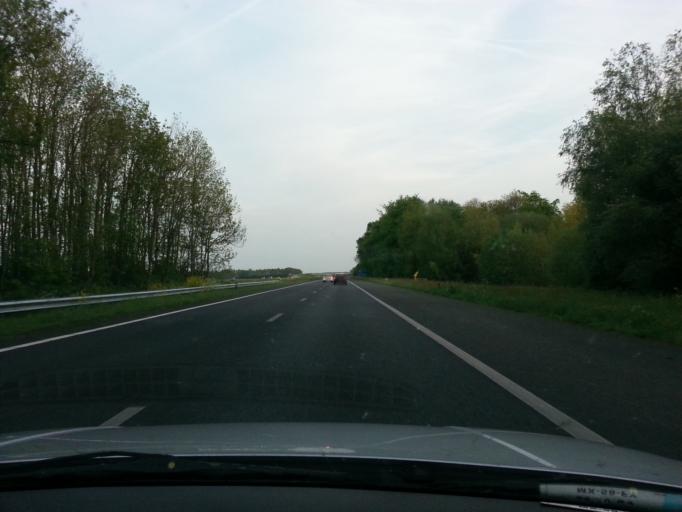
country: NL
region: Flevoland
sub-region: Gemeente Noordoostpolder
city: Emmeloord
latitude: 52.7777
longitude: 5.7597
